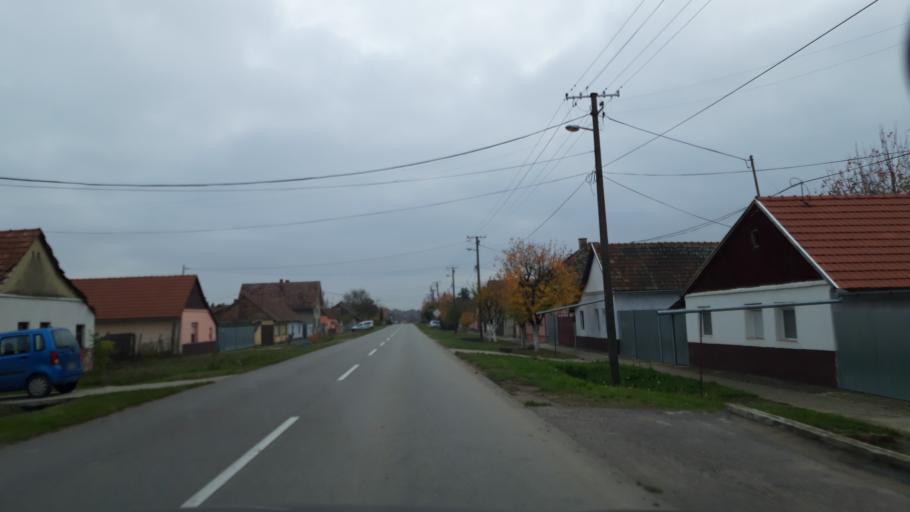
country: RS
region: Autonomna Pokrajina Vojvodina
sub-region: Severnobanatski Okrug
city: Novi Knezevac
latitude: 46.0572
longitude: 20.1002
